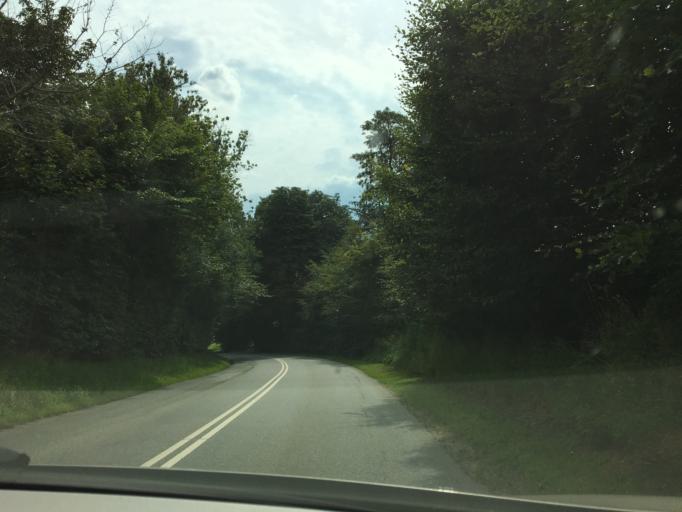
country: DK
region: Central Jutland
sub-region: Viborg Kommune
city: Stoholm
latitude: 56.4747
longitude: 9.1479
